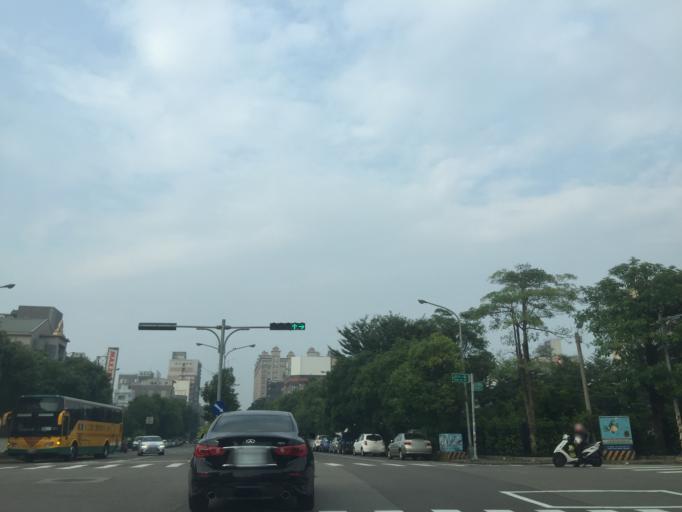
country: TW
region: Taiwan
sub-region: Hsinchu
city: Zhubei
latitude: 24.8200
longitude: 121.0127
